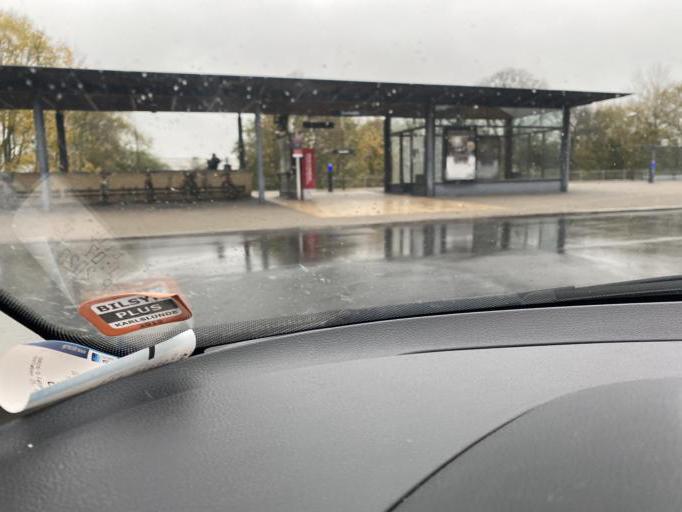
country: DK
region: Zealand
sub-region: Kalundborg Kommune
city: Svebolle
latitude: 55.6521
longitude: 11.2914
